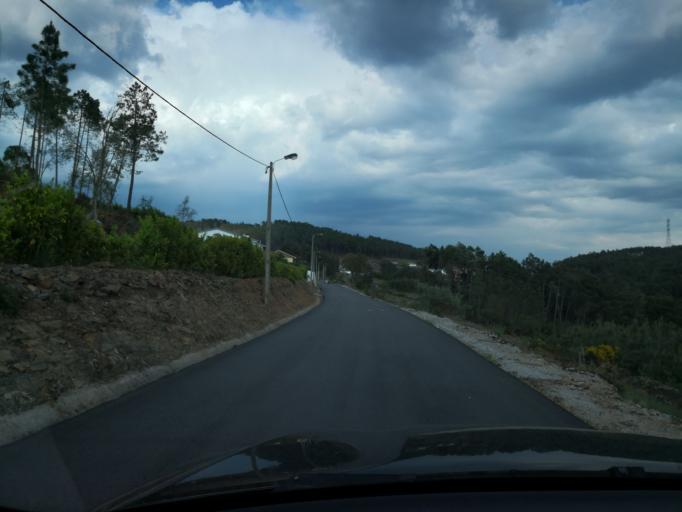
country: PT
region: Vila Real
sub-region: Sabrosa
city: Vilela
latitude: 41.2219
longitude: -7.6806
